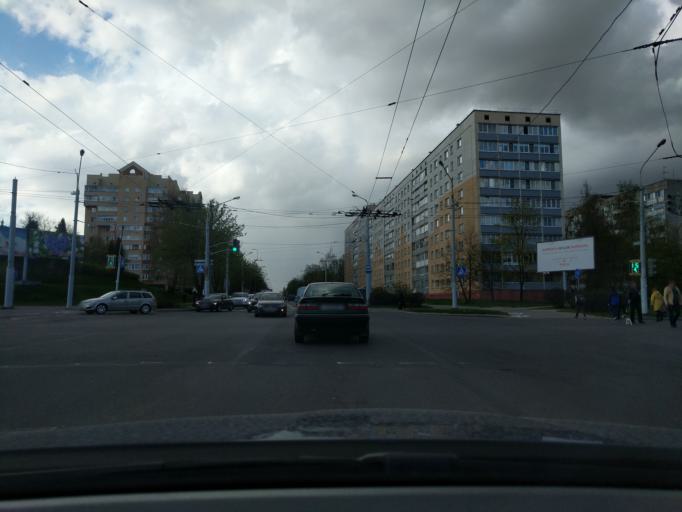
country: BY
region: Minsk
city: Novoye Medvezhino
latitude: 53.9018
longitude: 27.4818
